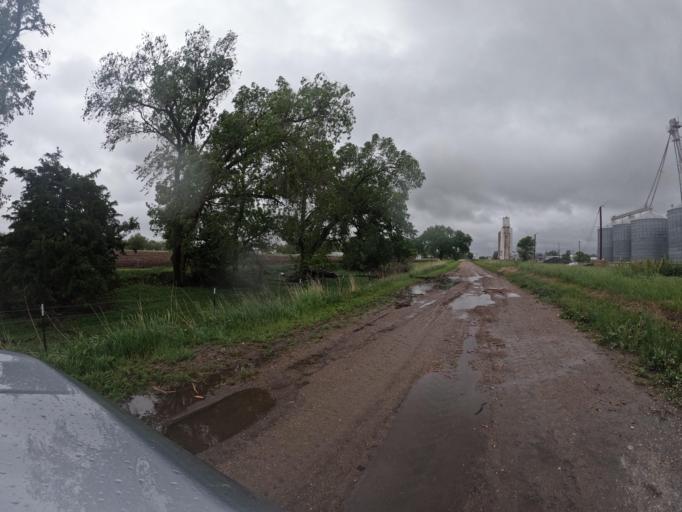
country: US
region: Nebraska
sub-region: Clay County
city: Harvard
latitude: 40.6161
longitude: -98.0913
